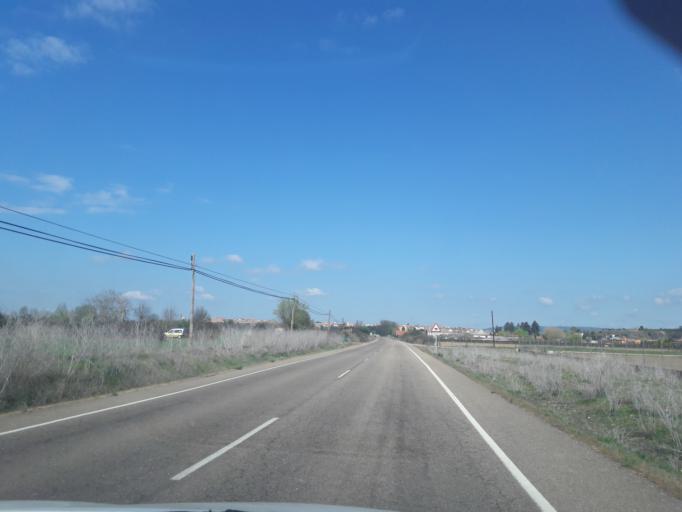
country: ES
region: Castille and Leon
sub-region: Provincia de Salamanca
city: Ciudad Rodrigo
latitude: 40.5840
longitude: -6.5084
